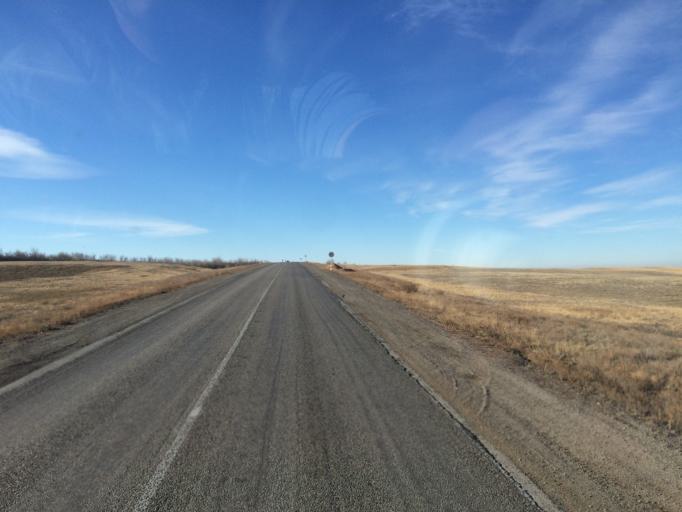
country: KZ
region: Aqtoebe
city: Aqtobe
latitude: 50.2825
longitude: 57.7573
